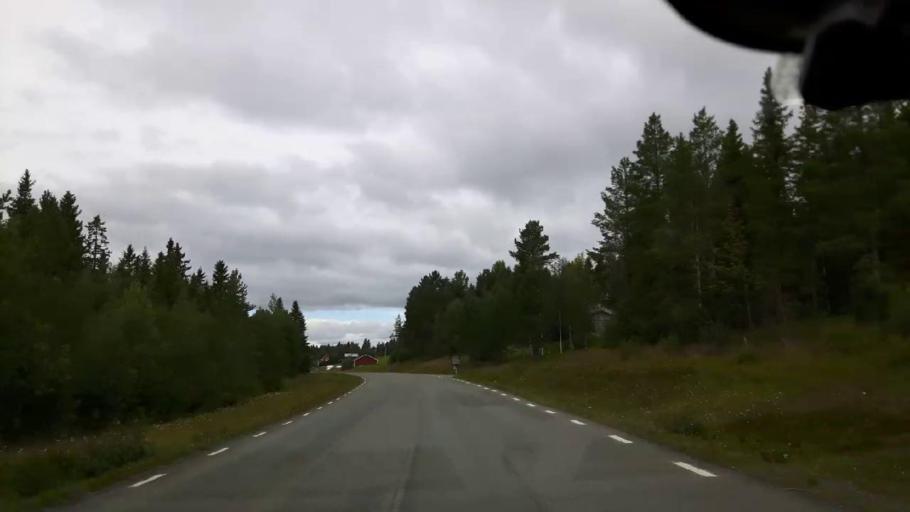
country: SE
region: Jaemtland
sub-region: Krokoms Kommun
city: Valla
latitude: 63.5084
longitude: 13.8927
